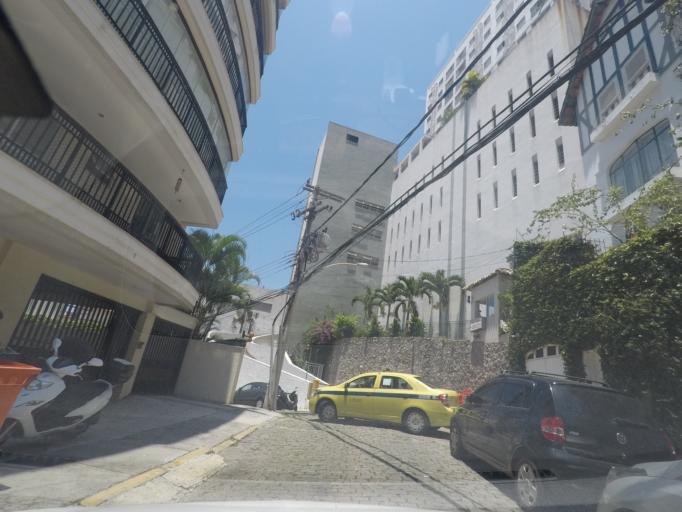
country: BR
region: Rio de Janeiro
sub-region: Rio De Janeiro
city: Rio de Janeiro
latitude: -22.9641
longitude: -43.1837
